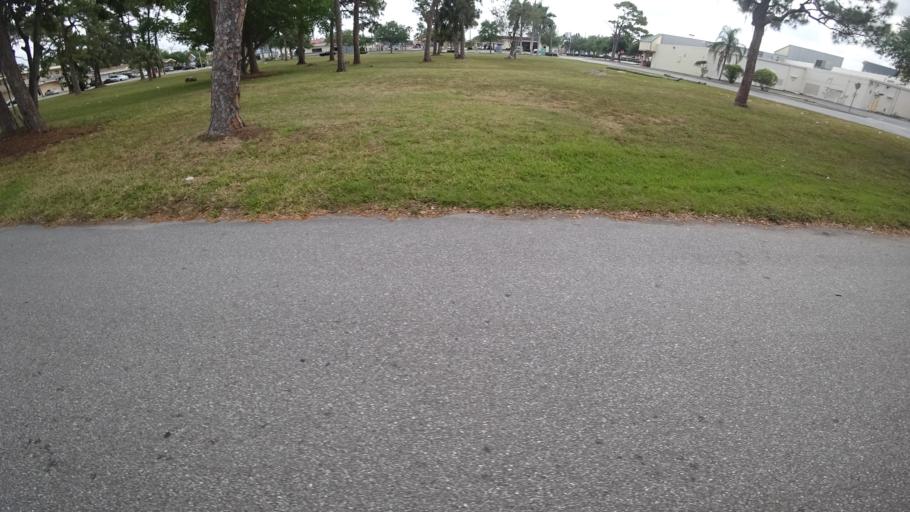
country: US
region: Florida
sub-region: Manatee County
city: Bayshore Gardens
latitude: 27.4396
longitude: -82.5774
